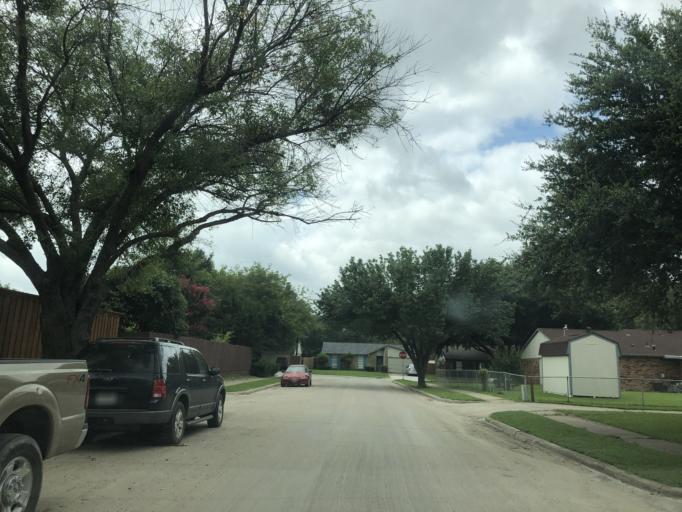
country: US
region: Texas
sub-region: Dallas County
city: Sunnyvale
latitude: 32.8443
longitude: -96.5678
